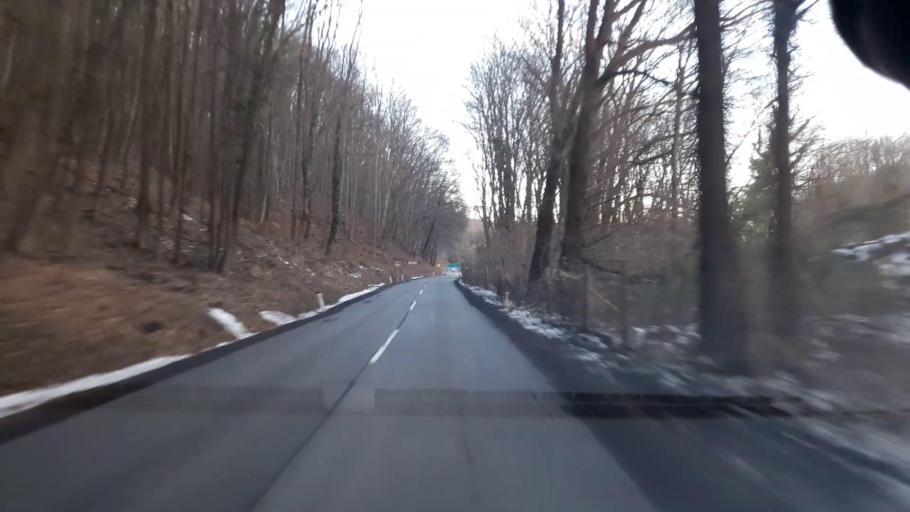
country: AT
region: Lower Austria
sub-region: Politischer Bezirk Wien-Umgebung
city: Klosterneuburg
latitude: 48.2748
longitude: 16.2753
